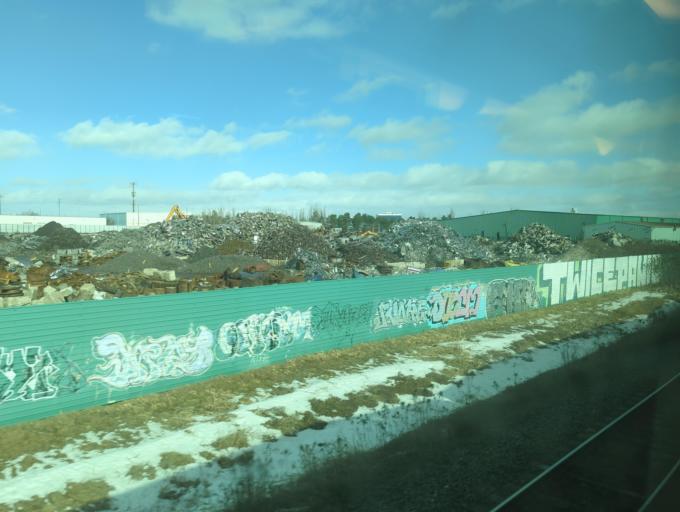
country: CA
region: Ontario
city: Burlington
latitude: 43.3720
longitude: -79.7689
